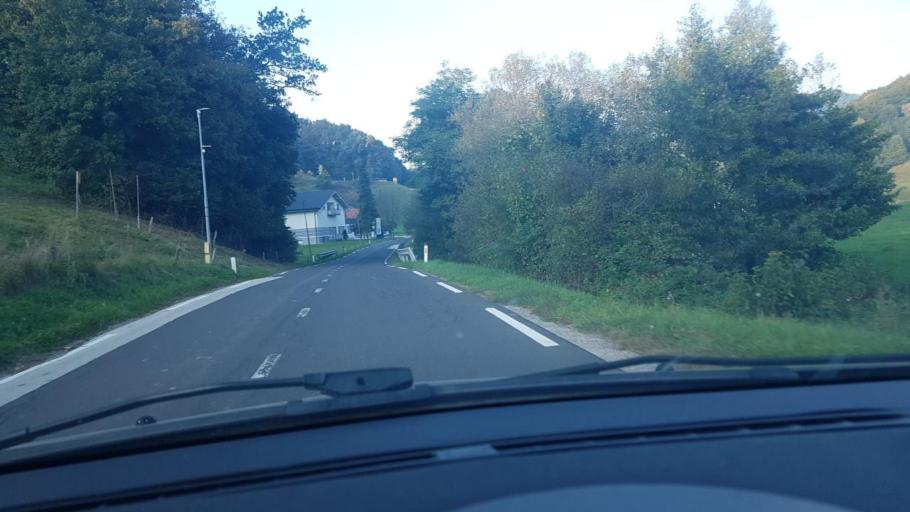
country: SI
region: Makole
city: Makole
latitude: 46.2876
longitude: 15.7151
